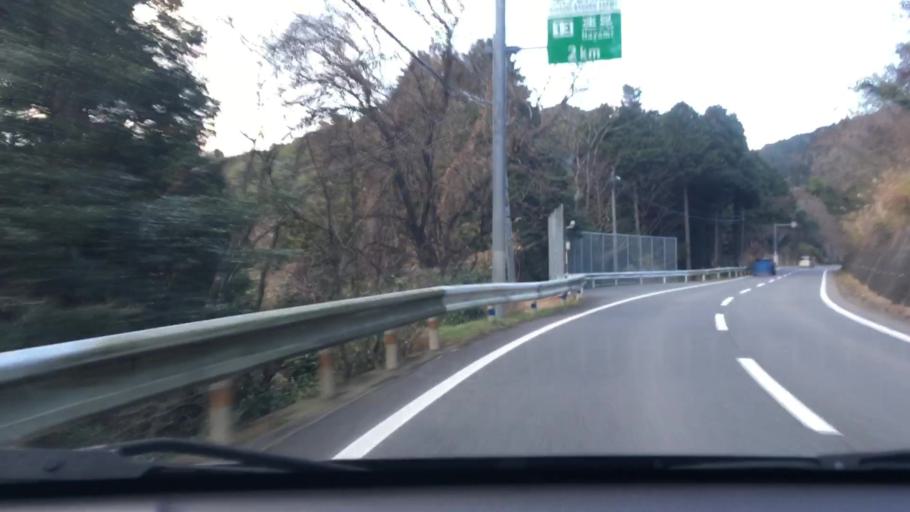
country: JP
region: Oita
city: Hiji
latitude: 33.3663
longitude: 131.4666
